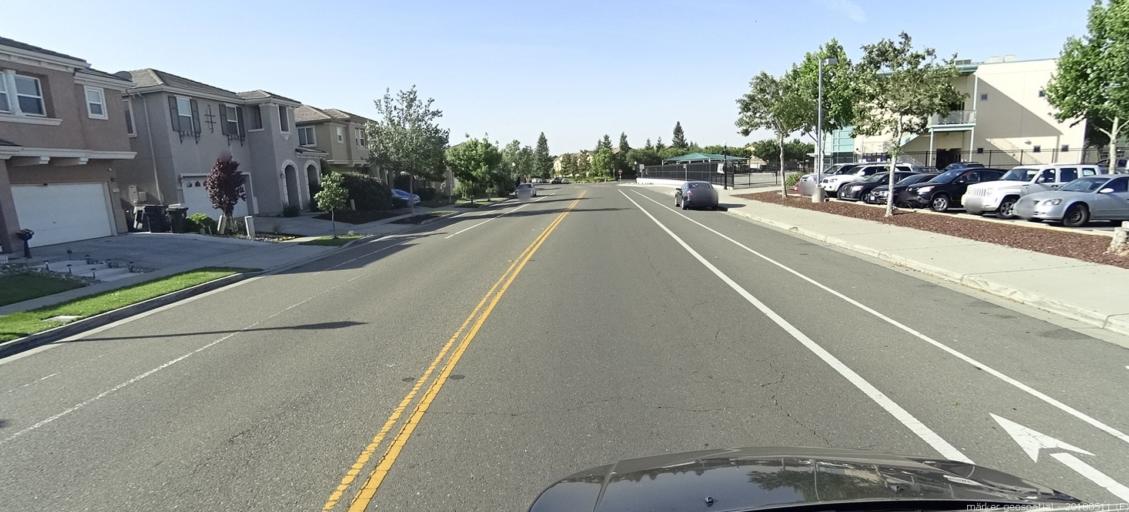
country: US
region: California
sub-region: Sacramento County
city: Elverta
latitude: 38.6675
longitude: -121.5304
